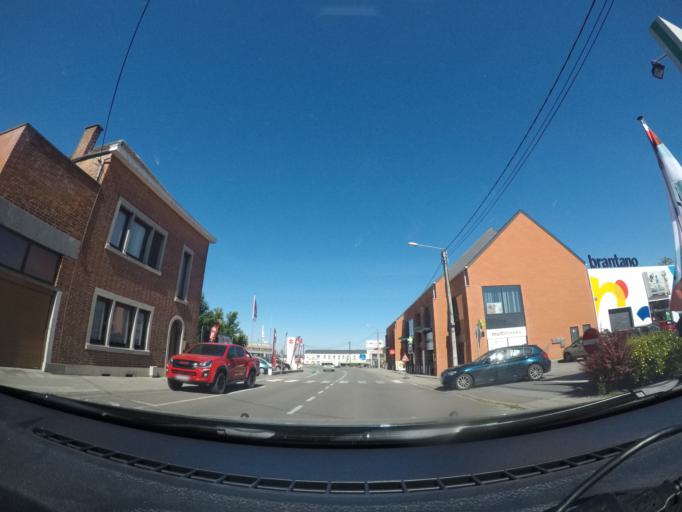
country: BE
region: Wallonia
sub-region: Province de Namur
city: Philippeville
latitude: 50.1964
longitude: 4.5379
